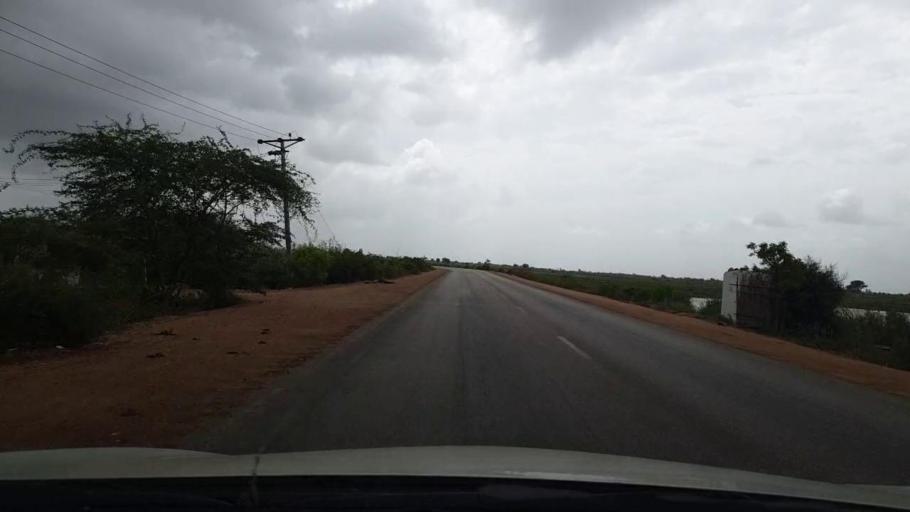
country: PK
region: Sindh
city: Mirpur Batoro
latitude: 24.5986
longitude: 68.2224
